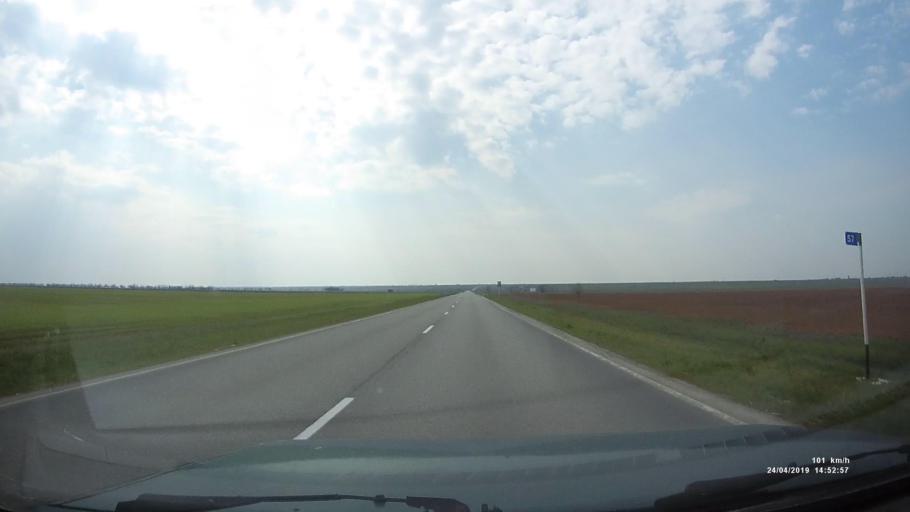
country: RU
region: Rostov
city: Remontnoye
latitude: 46.5308
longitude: 43.6697
